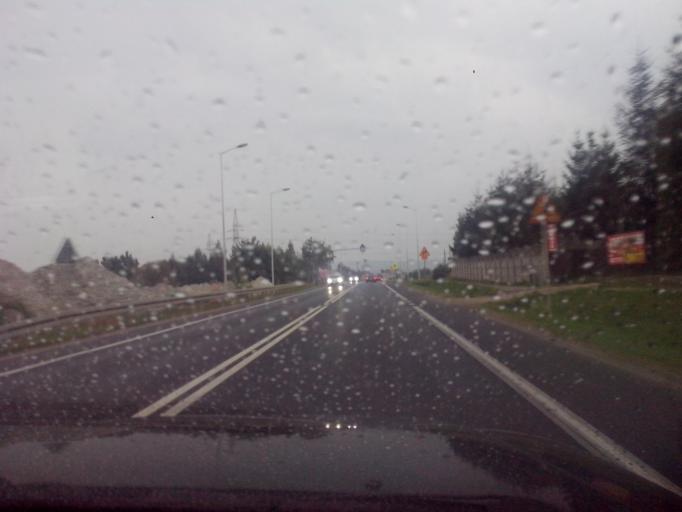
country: PL
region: Subcarpathian Voivodeship
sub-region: Powiat rzeszowski
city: Boguchwala
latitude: 49.9978
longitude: 21.9570
